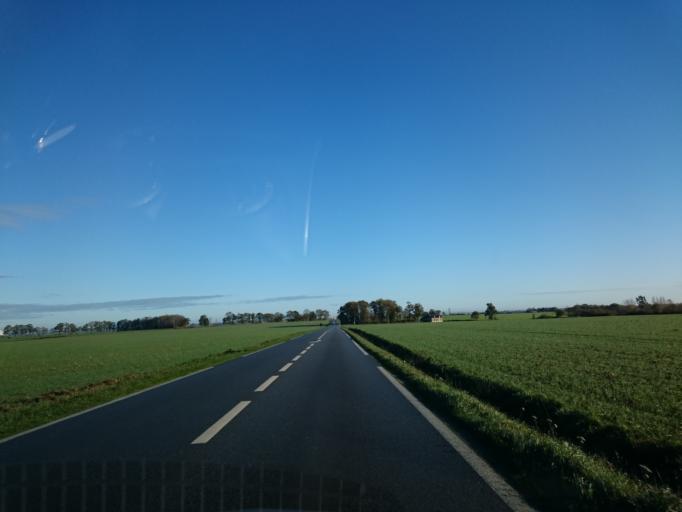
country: FR
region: Brittany
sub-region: Departement d'Ille-et-Vilaine
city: Tresboeuf
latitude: 47.9296
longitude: -1.5480
